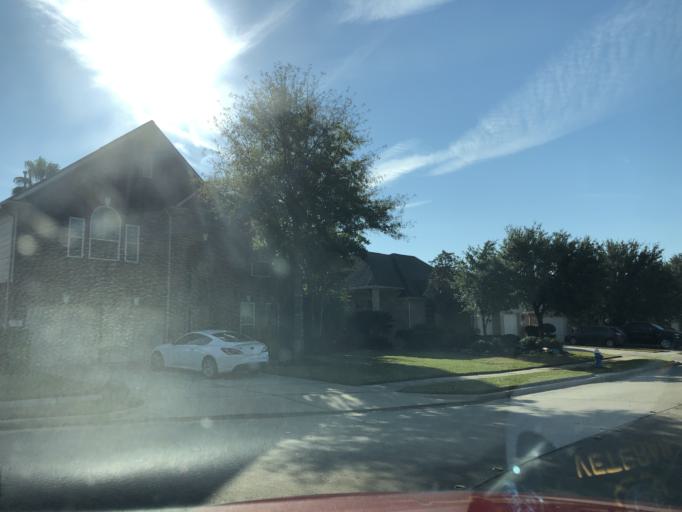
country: US
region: Texas
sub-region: Harris County
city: Tomball
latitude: 30.0322
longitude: -95.5609
